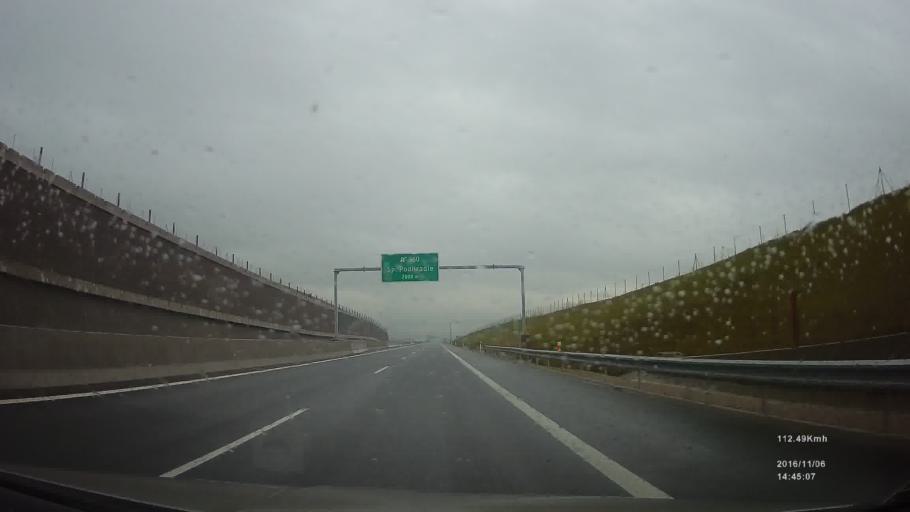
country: SK
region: Presovsky
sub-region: Okres Presov
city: Levoca
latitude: 49.0093
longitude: 20.6693
